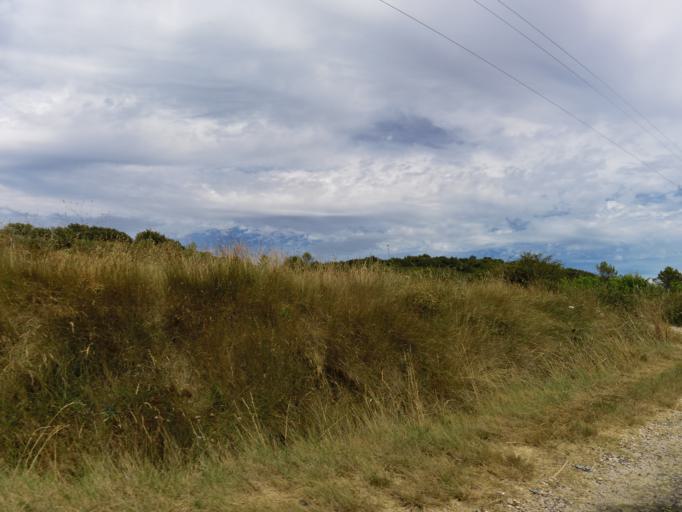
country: FR
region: Languedoc-Roussillon
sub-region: Departement du Gard
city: Congenies
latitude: 43.8061
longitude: 4.1510
